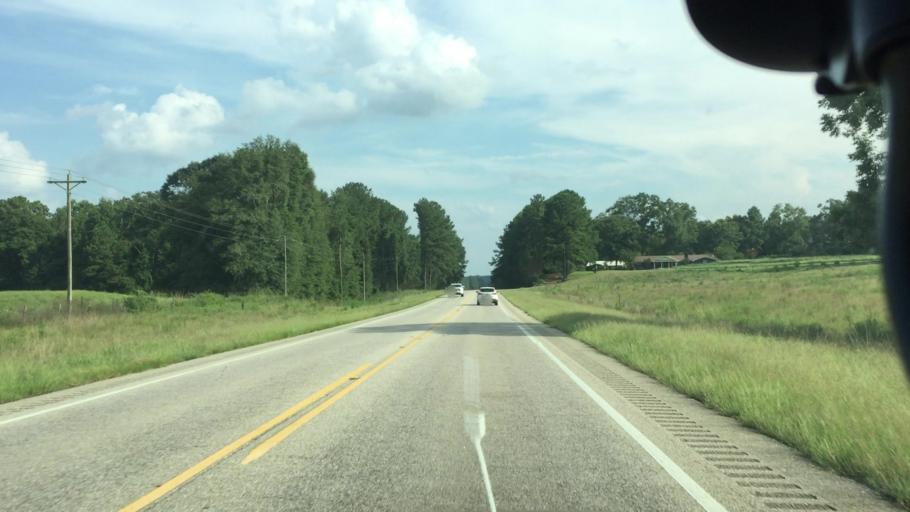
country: US
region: Alabama
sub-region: Pike County
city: Brundidge
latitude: 31.6517
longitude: -85.9502
